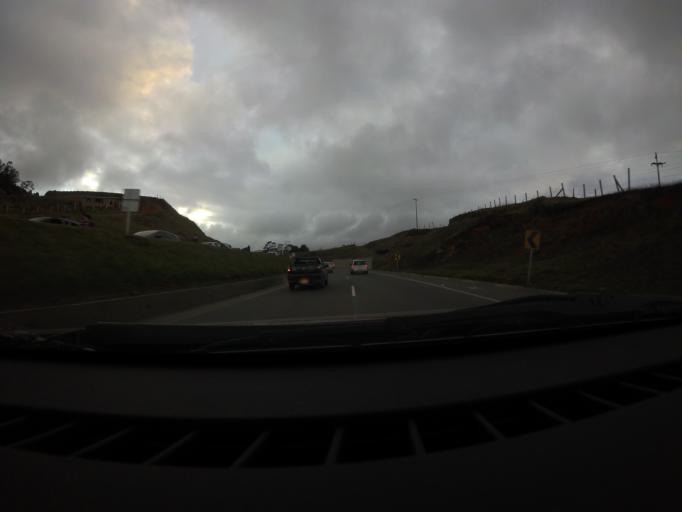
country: CO
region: Boyaca
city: Samaca
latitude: 5.4399
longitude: -73.4412
